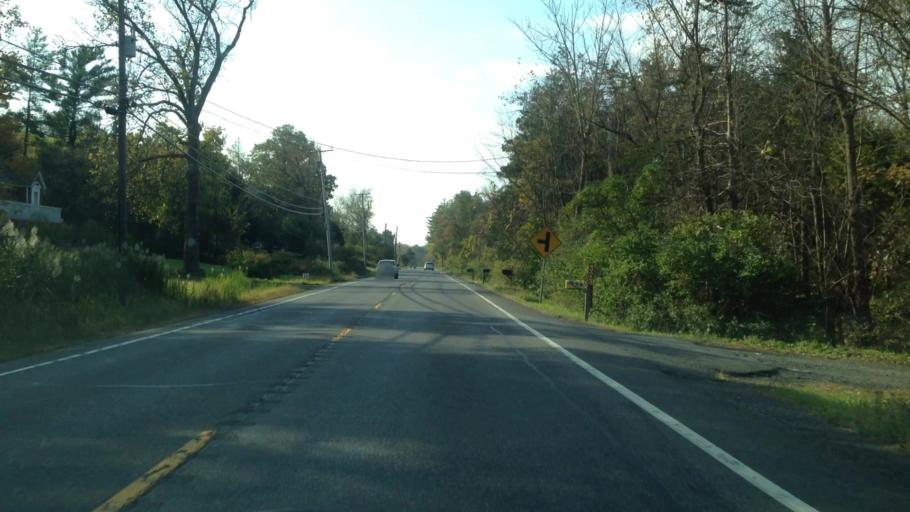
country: US
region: New York
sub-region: Ulster County
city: New Paltz
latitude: 41.7777
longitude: -74.0737
